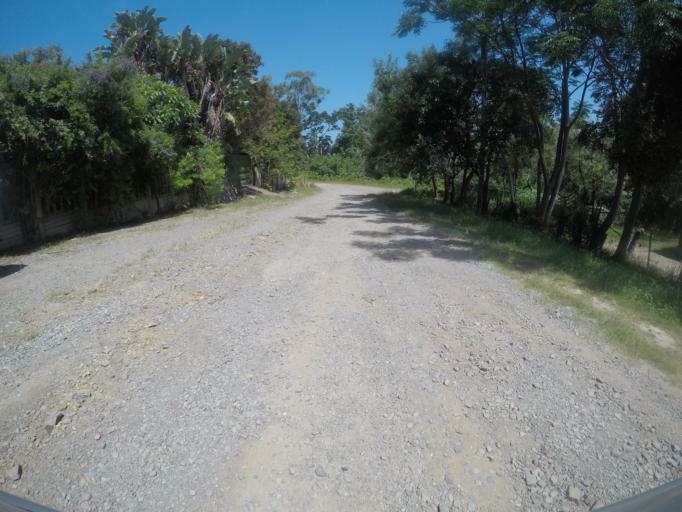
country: ZA
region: Eastern Cape
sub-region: Buffalo City Metropolitan Municipality
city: East London
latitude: -32.9695
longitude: 27.8549
